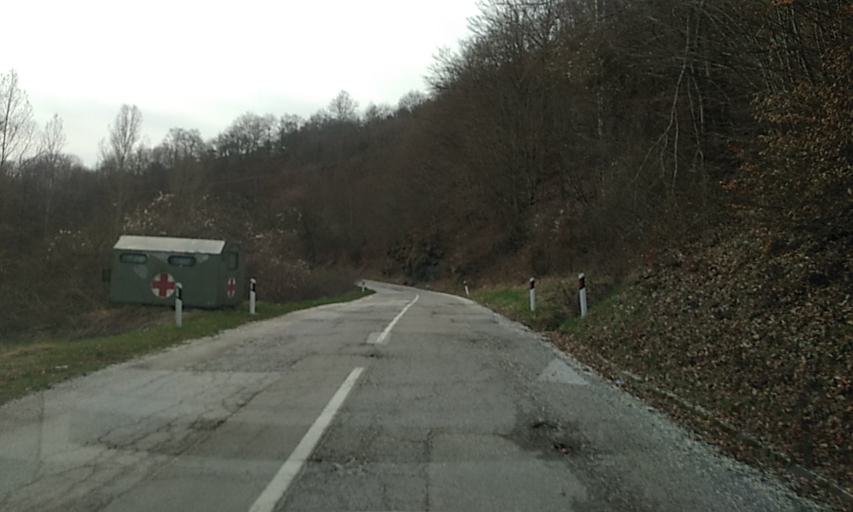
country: RS
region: Central Serbia
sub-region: Pcinjski Okrug
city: Bosilegrad
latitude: 42.5456
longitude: 22.3974
